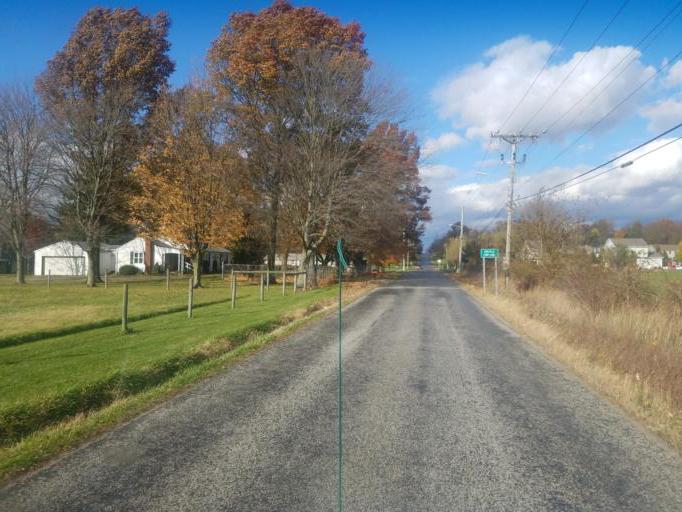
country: US
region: Ohio
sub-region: Wayne County
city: Orrville
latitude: 40.8281
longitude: -81.7745
